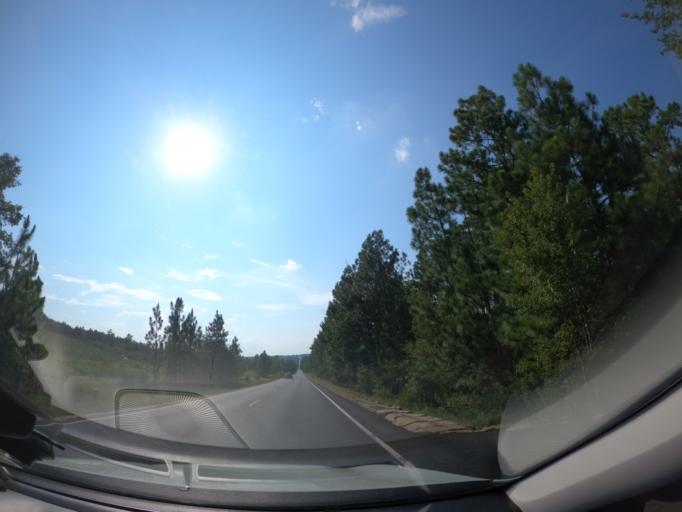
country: US
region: South Carolina
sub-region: Aiken County
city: Jackson
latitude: 33.4048
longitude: -81.7772
